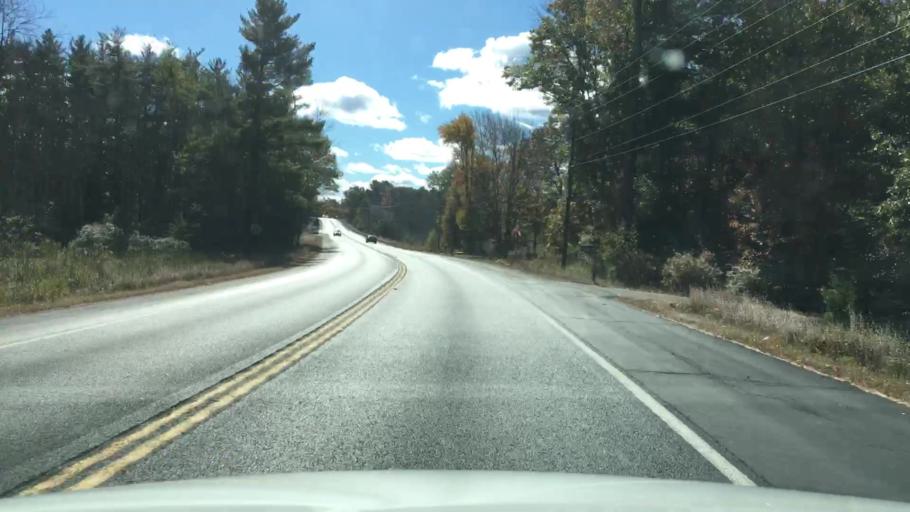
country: US
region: Maine
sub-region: York County
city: Alfred
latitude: 43.4451
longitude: -70.7302
